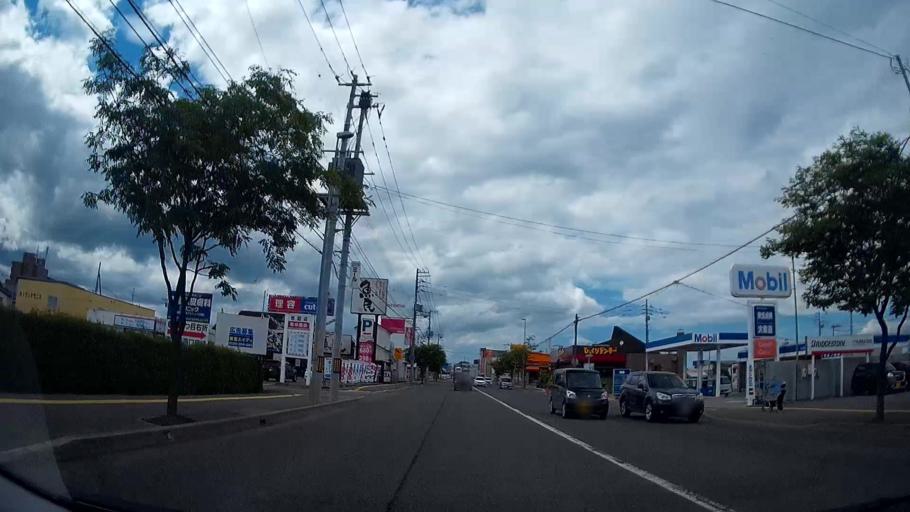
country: JP
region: Hokkaido
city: Chitose
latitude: 42.8747
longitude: 141.5839
